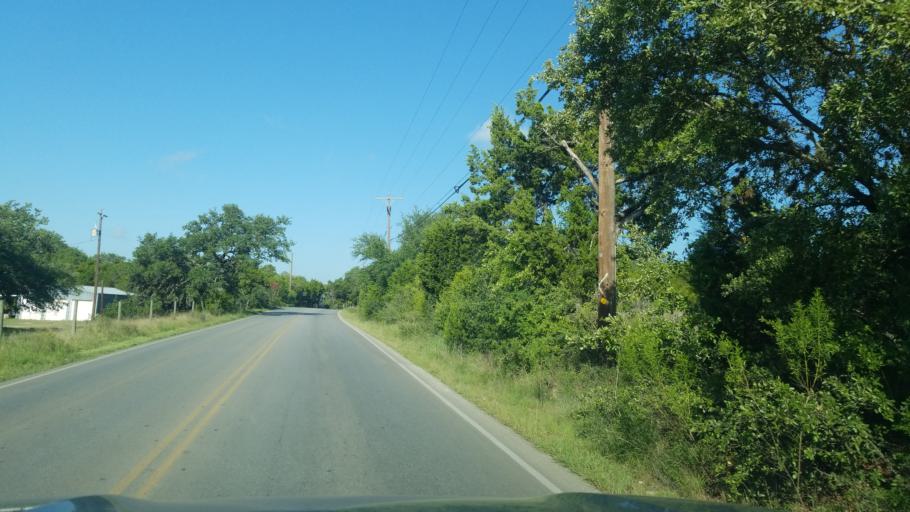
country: US
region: Texas
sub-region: Comal County
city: Bulverde
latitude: 29.7428
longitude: -98.4368
